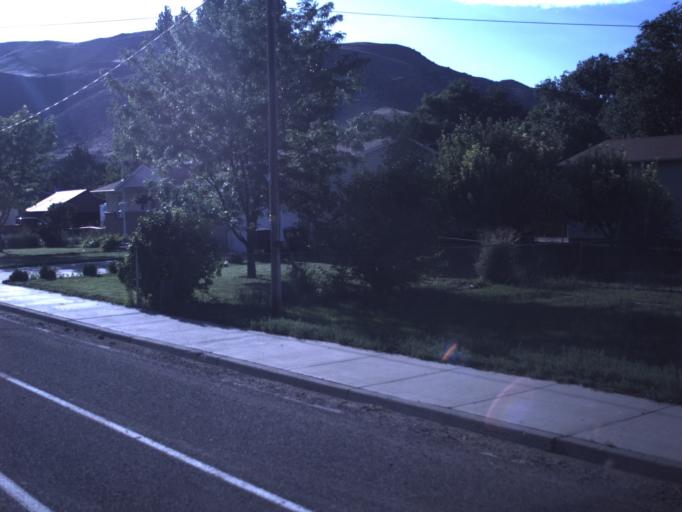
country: US
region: Utah
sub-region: Sevier County
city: Monroe
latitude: 38.6831
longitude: -112.1458
